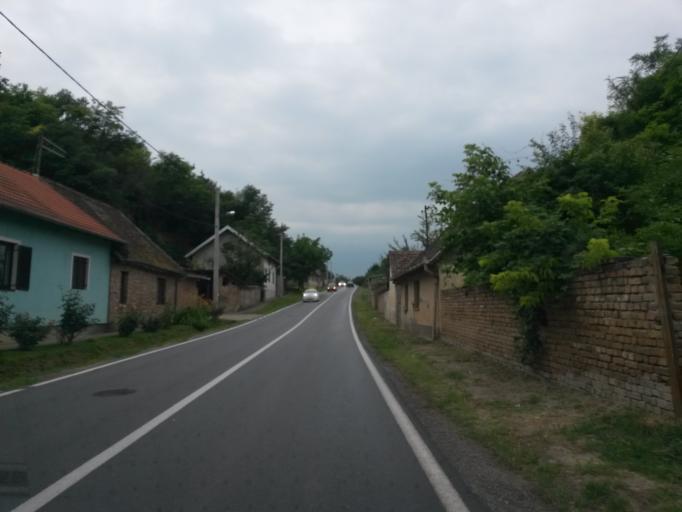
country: HR
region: Vukovarsko-Srijemska
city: Bapska
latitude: 45.2328
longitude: 19.2941
